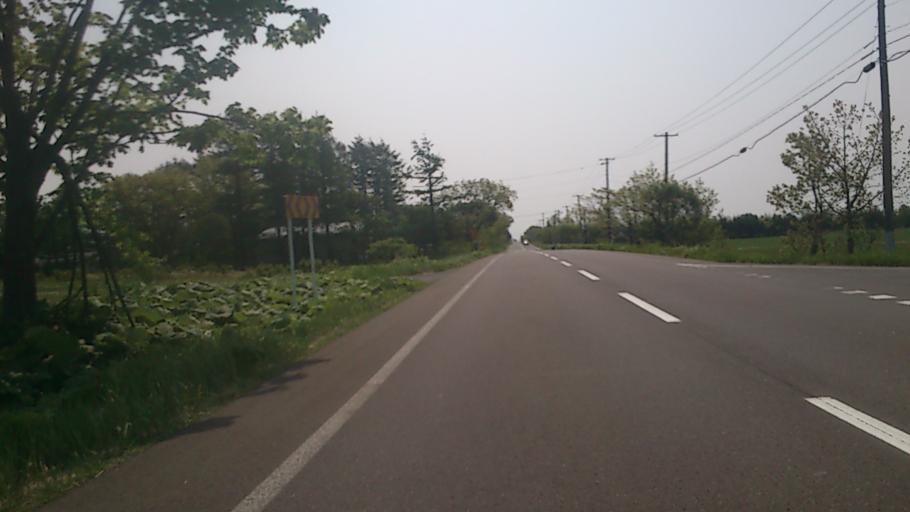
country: JP
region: Hokkaido
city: Shibetsu
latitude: 43.3835
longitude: 144.8331
